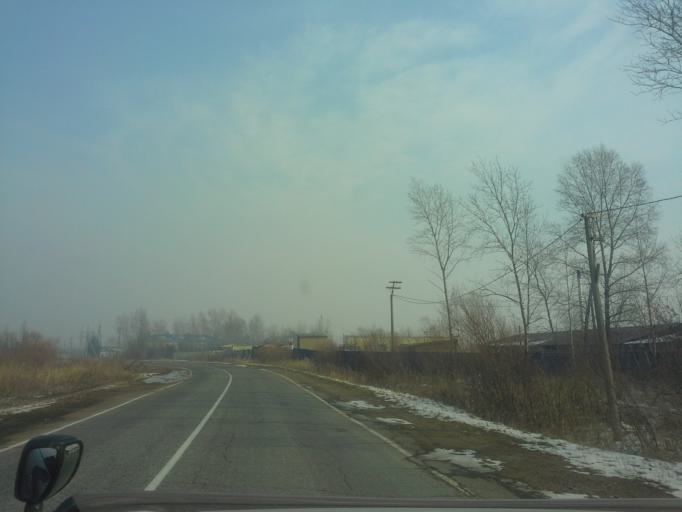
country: RU
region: Jewish Autonomous Oblast
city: Priamurskiy
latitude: 48.5368
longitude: 134.9049
